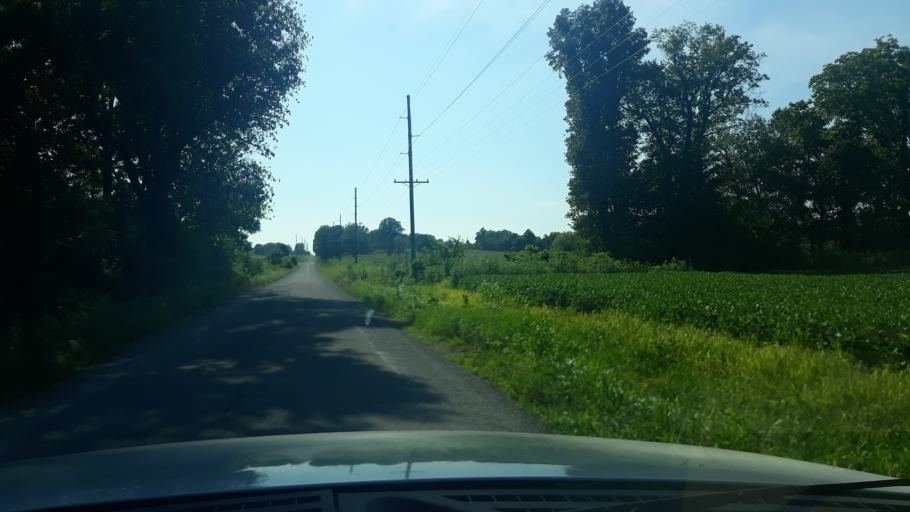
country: US
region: Illinois
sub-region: Saline County
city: Eldorado
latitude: 37.8629
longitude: -88.5262
